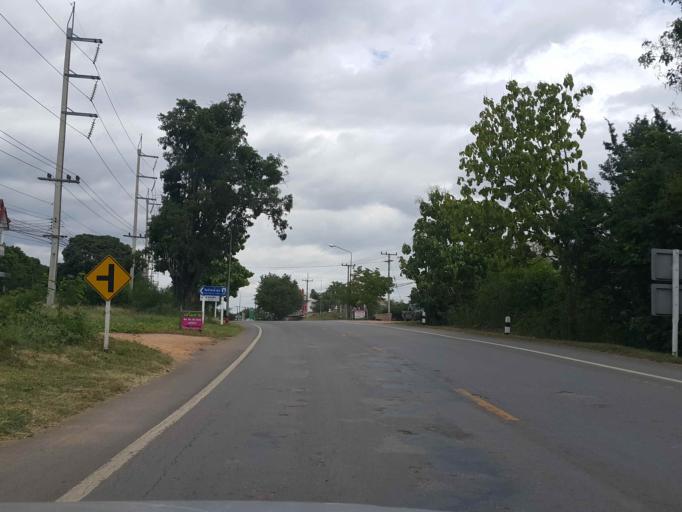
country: TH
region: Lamphun
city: Thung Hua Chang
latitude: 17.9913
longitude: 98.8755
